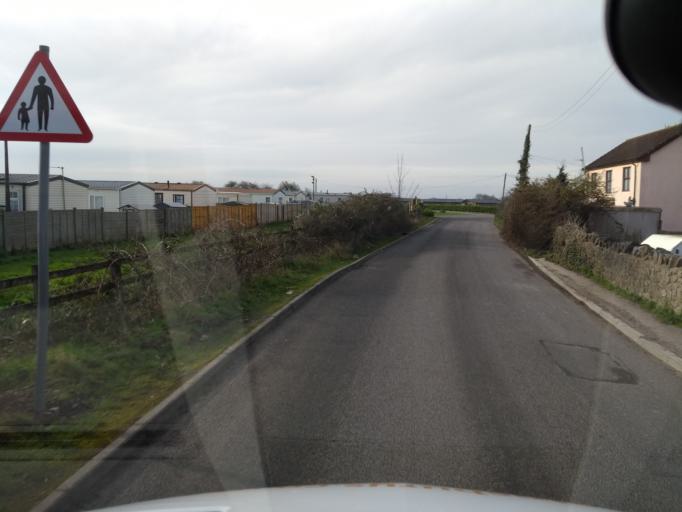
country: GB
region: England
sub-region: North Somerset
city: Bleadon
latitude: 51.3082
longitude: -2.9604
